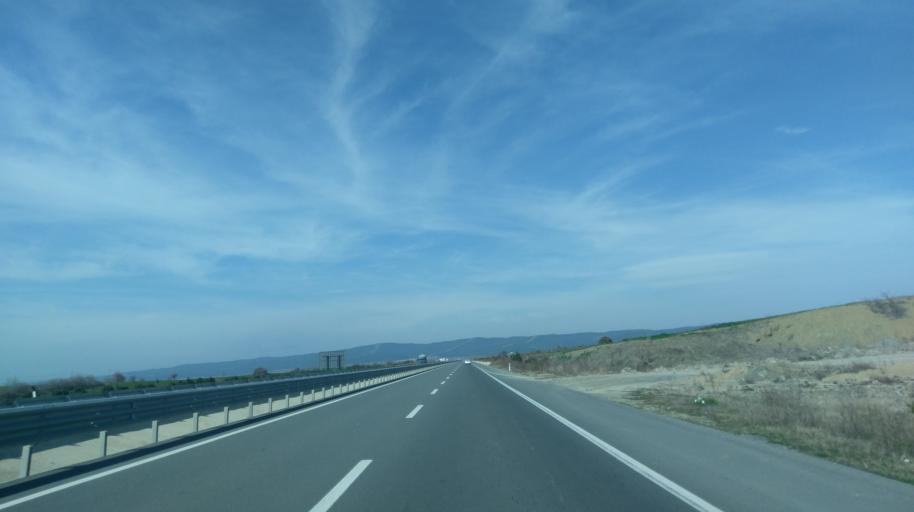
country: TR
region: Canakkale
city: Evrese
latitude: 40.6453
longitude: 26.8479
